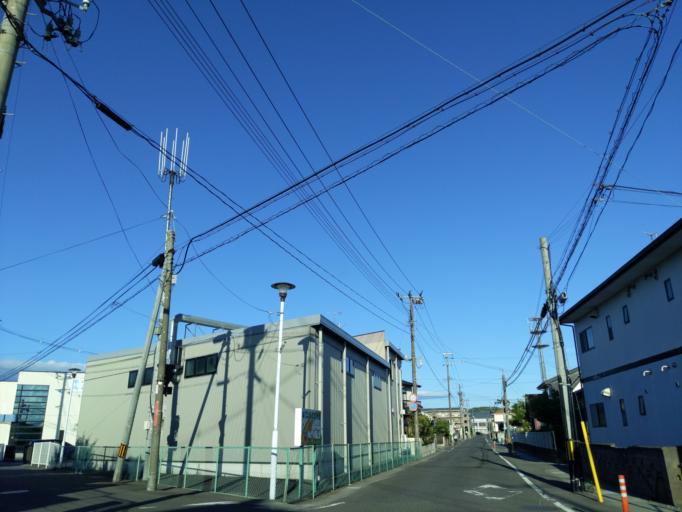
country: JP
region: Fukushima
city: Koriyama
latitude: 37.3933
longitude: 140.4032
